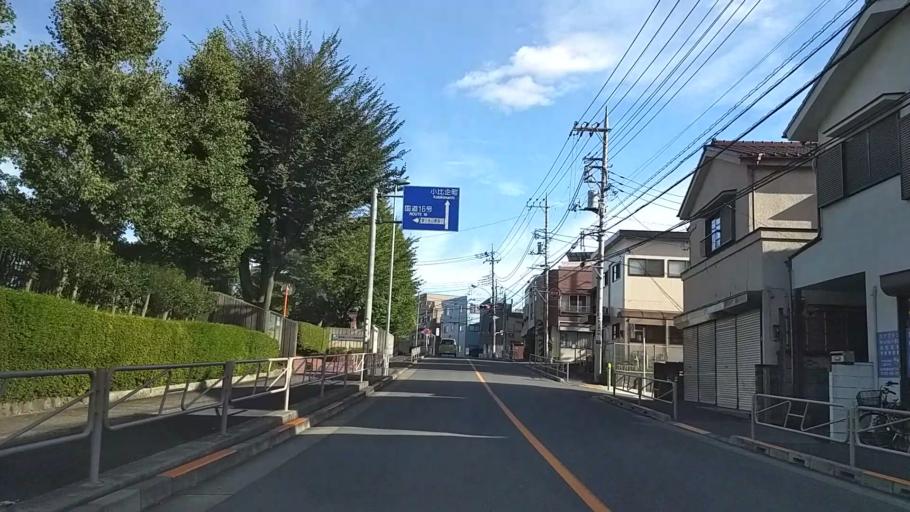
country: JP
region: Tokyo
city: Hachioji
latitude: 35.6546
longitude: 139.3163
